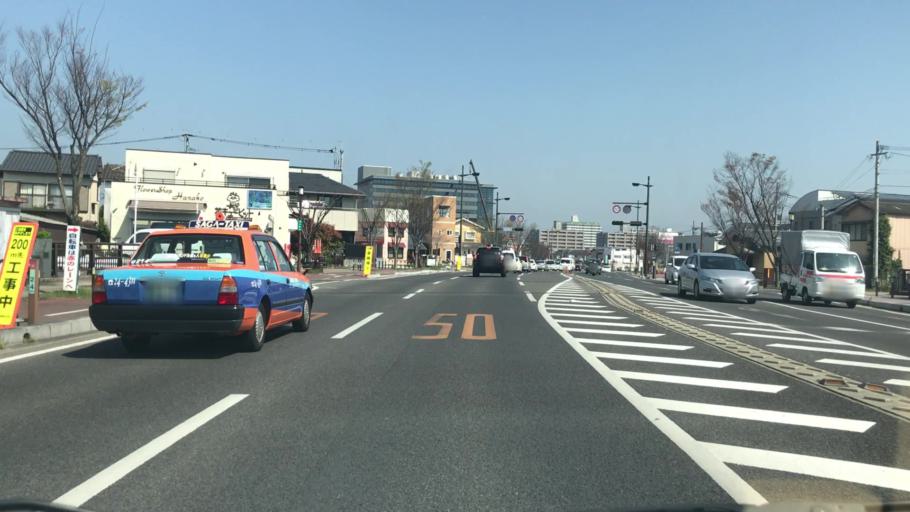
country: JP
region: Saga Prefecture
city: Saga-shi
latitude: 33.2530
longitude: 130.2922
